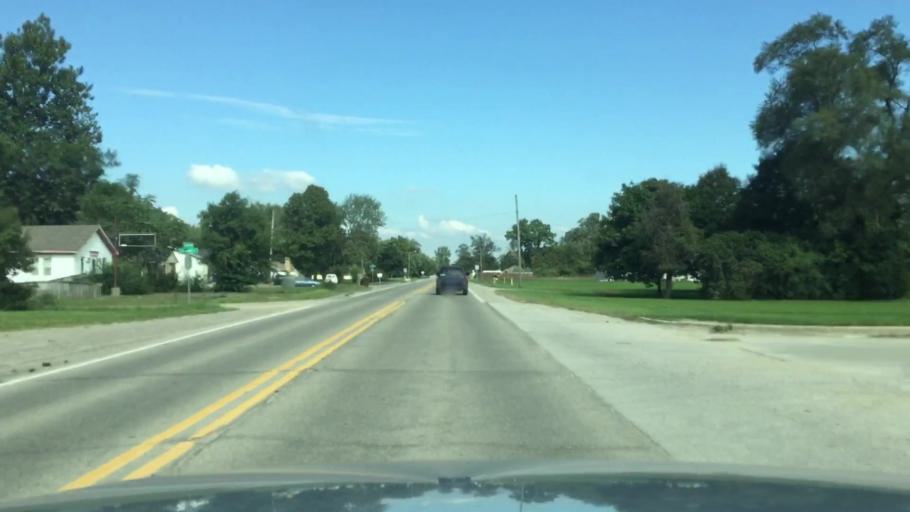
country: US
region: Michigan
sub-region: Wayne County
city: Belleville
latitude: 42.1908
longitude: -83.4835
